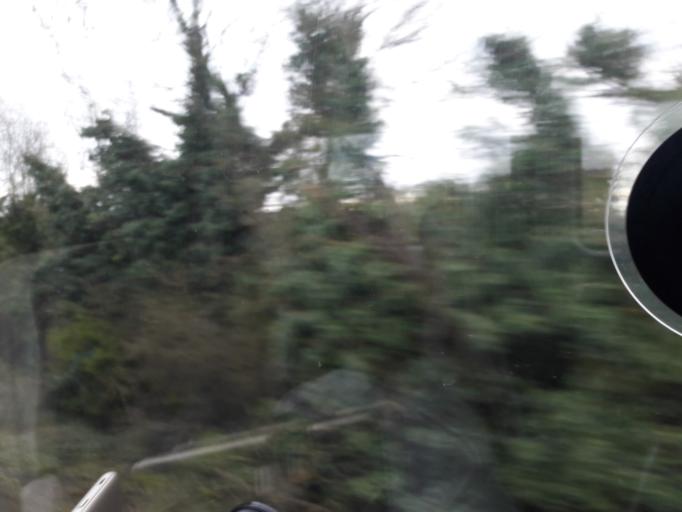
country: IE
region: Leinster
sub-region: An Longfort
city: Granard
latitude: 53.6626
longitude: -7.4599
